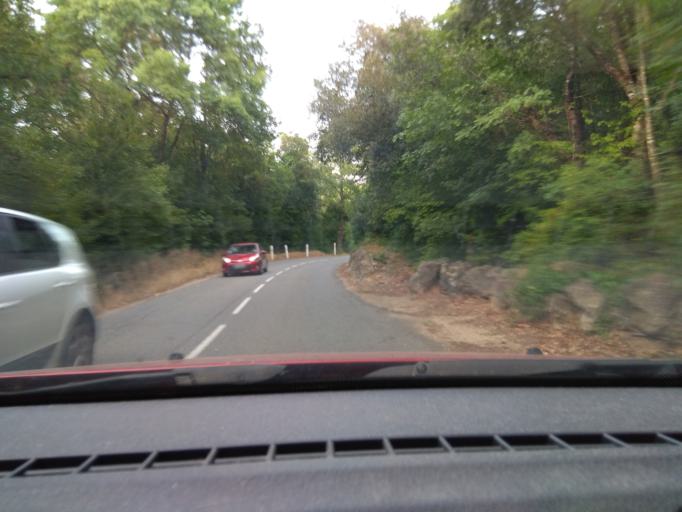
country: FR
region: Provence-Alpes-Cote d'Azur
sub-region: Departement des Alpes-Maritimes
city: Le Rouret
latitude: 43.6794
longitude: 7.0482
